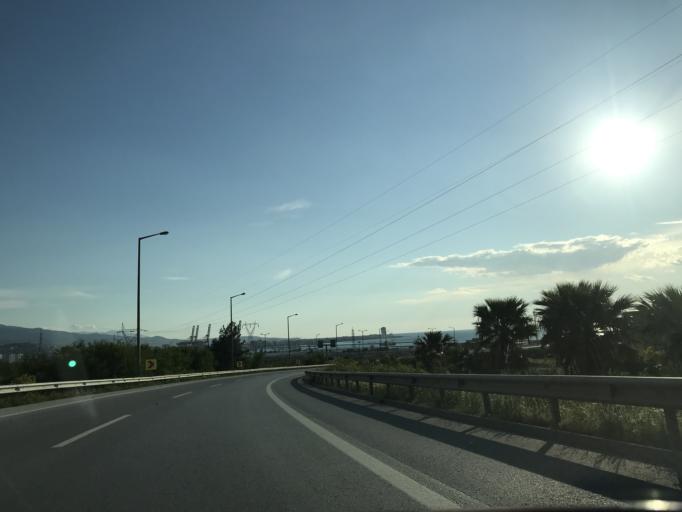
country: TR
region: Hatay
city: Guzelkoy
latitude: 36.6078
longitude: 36.2091
